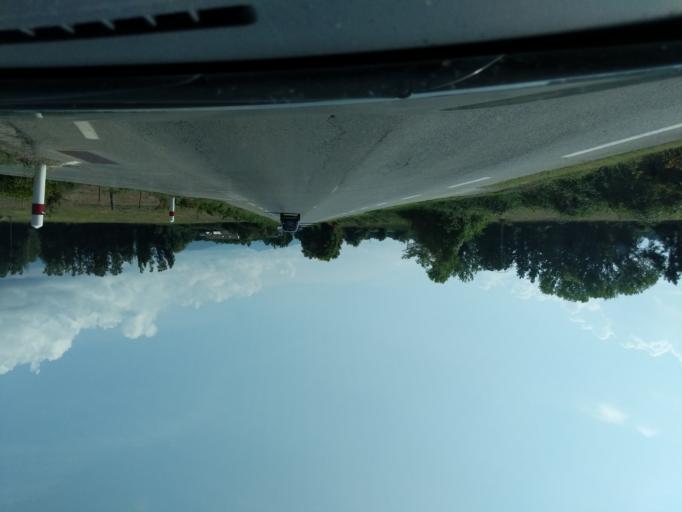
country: FR
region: Corsica
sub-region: Departement de la Haute-Corse
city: Ghisonaccia
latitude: 41.9759
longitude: 9.3994
